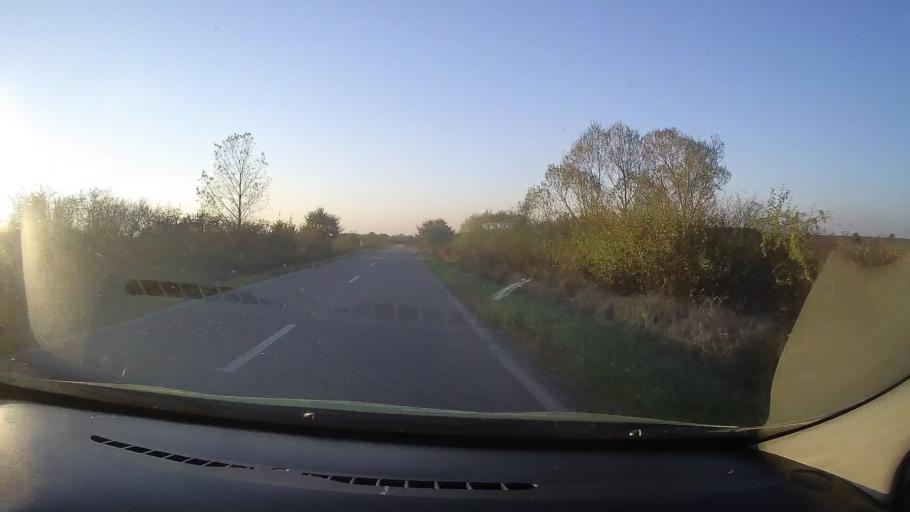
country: RO
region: Timis
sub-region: Comuna Traian Vuia
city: Traian Vuia
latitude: 45.7891
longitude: 22.0766
